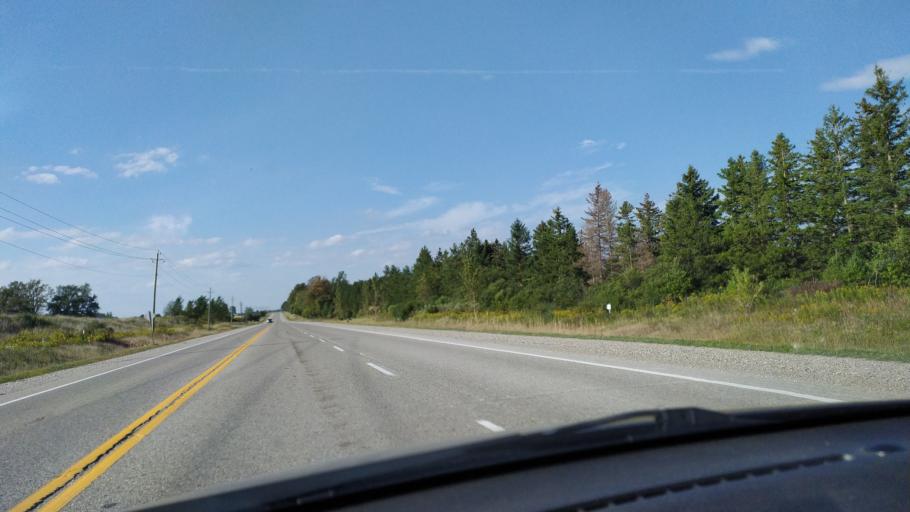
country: CA
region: Ontario
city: Ingersoll
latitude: 43.0768
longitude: -80.8605
